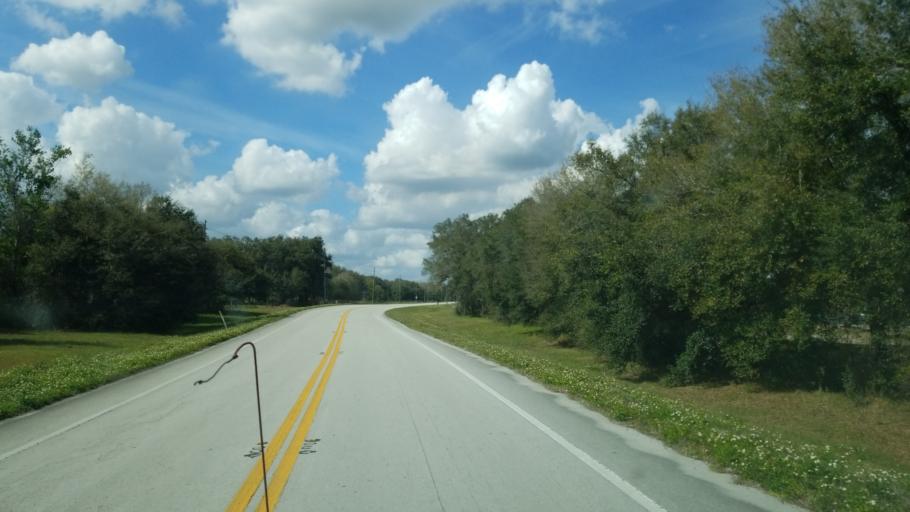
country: US
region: Florida
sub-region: Osceola County
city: Saint Cloud
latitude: 28.0221
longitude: -81.0344
